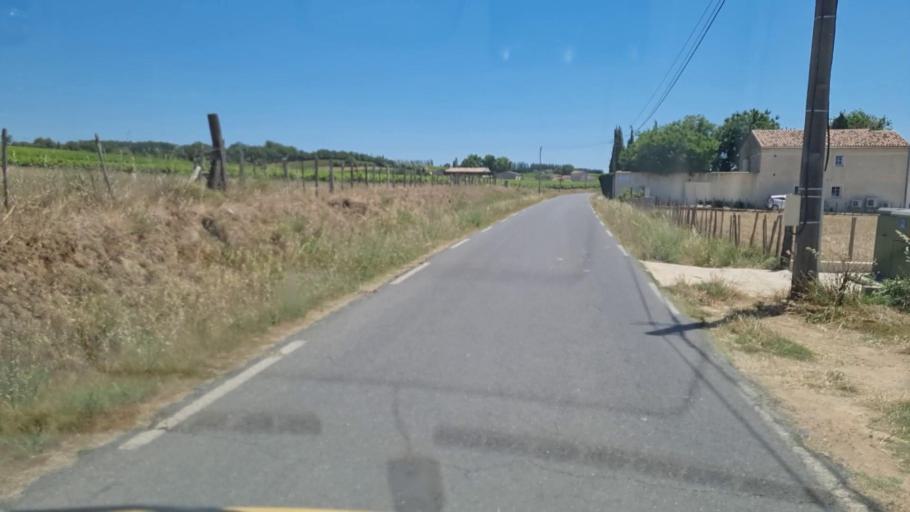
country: FR
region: Languedoc-Roussillon
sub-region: Departement du Gard
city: Le Cailar
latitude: 43.6626
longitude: 4.2575
